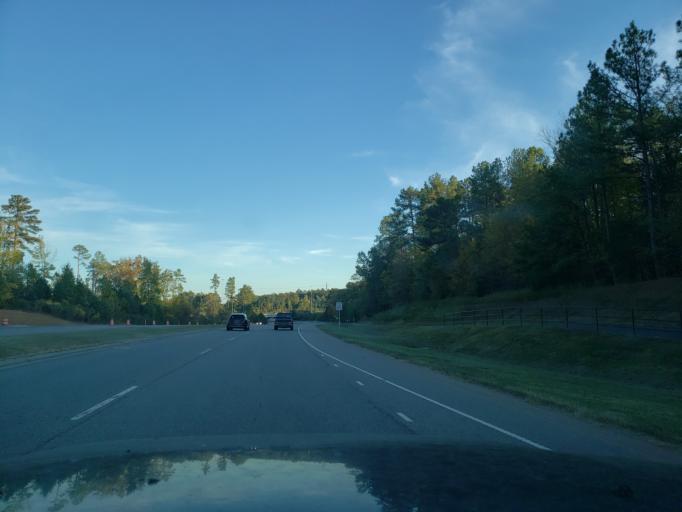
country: US
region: North Carolina
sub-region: Wake County
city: Morrisville
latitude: 35.8560
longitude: -78.8674
